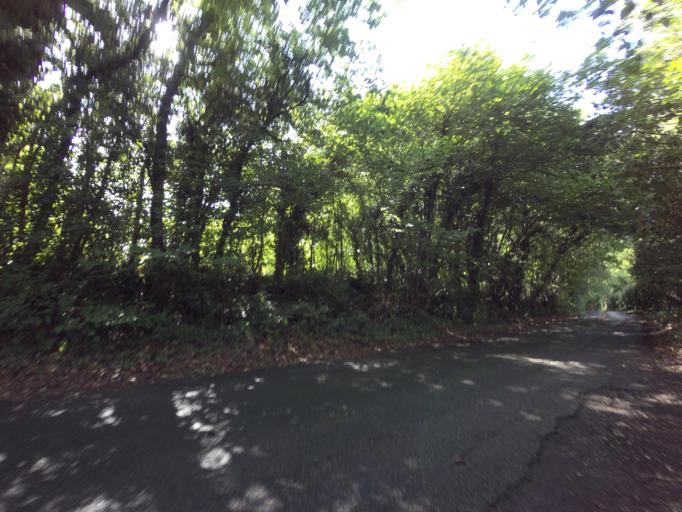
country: GB
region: England
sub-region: Kent
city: Borough Green
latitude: 51.2718
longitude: 0.2811
